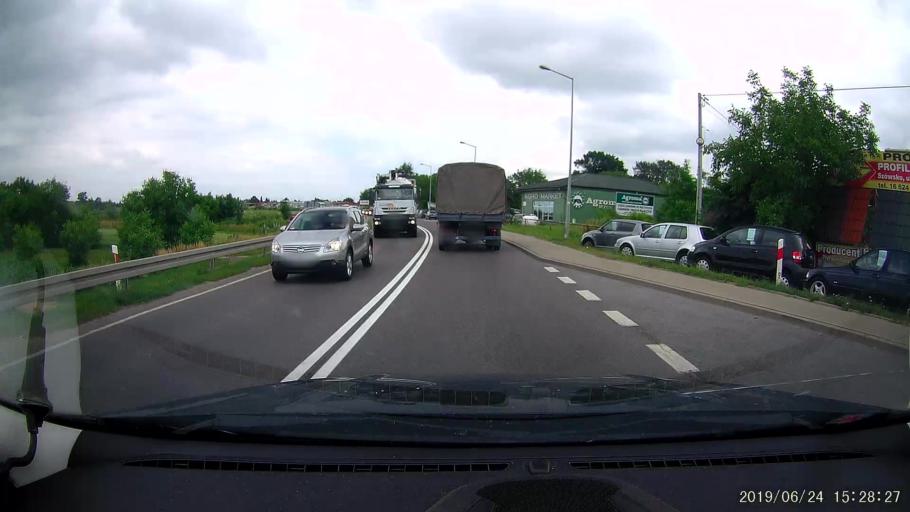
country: PL
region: Subcarpathian Voivodeship
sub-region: Powiat jaroslawski
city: Jaroslaw
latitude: 50.0216
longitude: 22.7081
